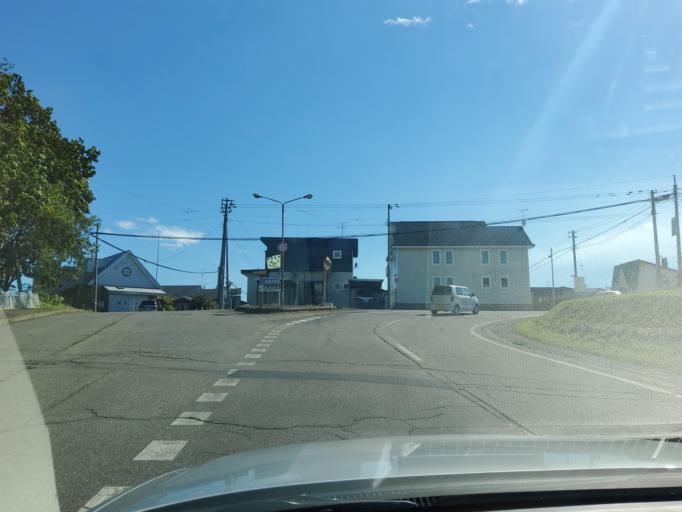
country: JP
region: Hokkaido
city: Obihiro
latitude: 42.9520
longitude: 143.1976
